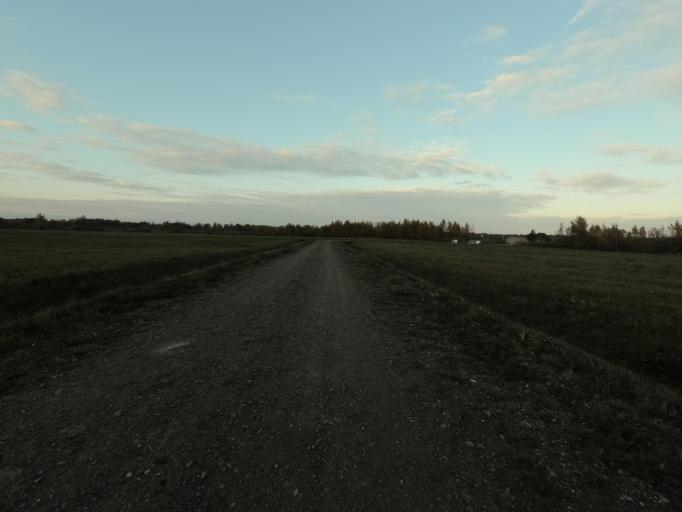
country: RU
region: Leningrad
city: Mga
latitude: 59.7888
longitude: 31.2001
